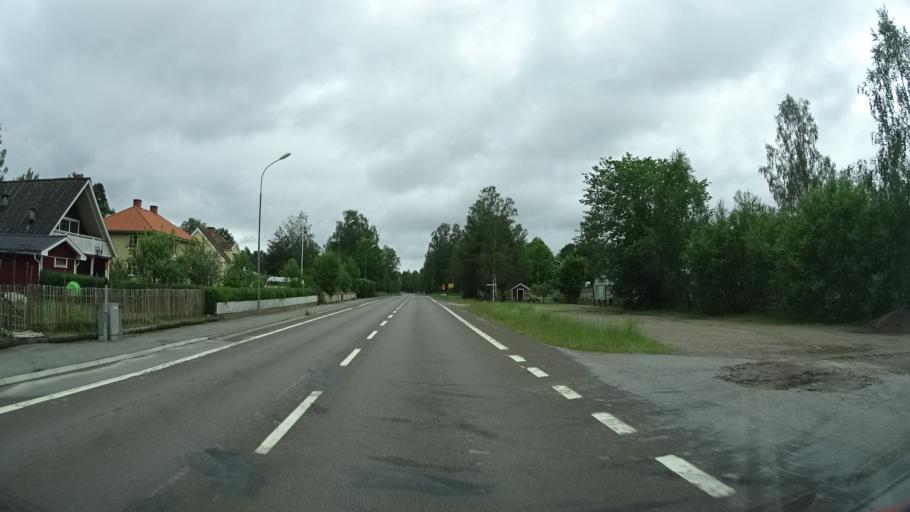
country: SE
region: Kalmar
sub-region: Hultsfreds Kommun
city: Hultsfred
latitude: 57.5519
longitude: 15.7210
